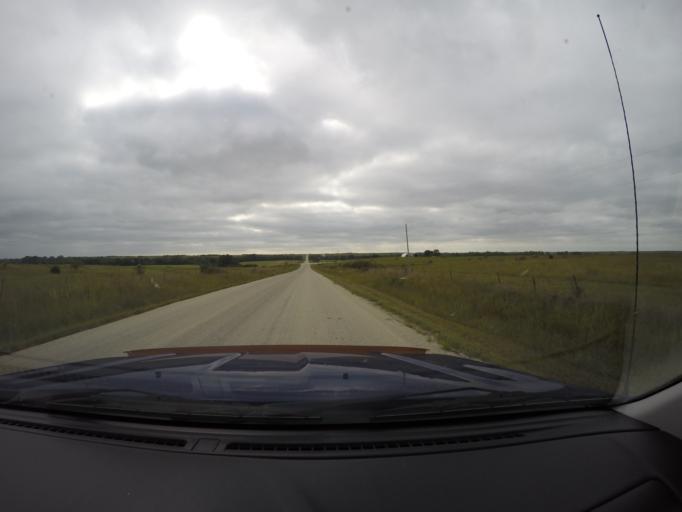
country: US
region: Kansas
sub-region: Dickinson County
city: Herington
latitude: 38.7974
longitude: -96.7754
